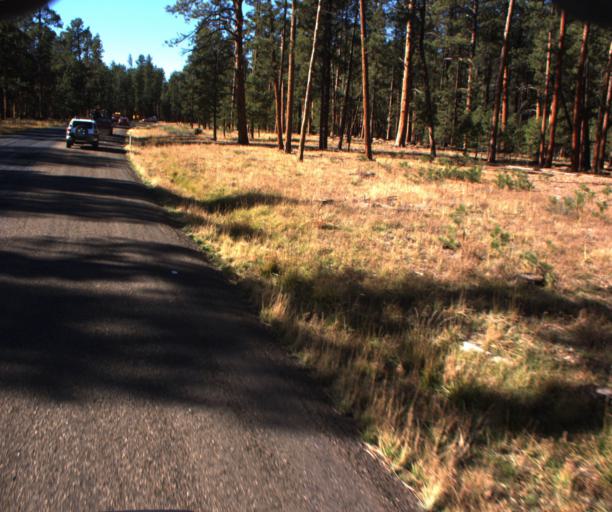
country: US
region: Arizona
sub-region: Coconino County
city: Fredonia
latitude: 36.7186
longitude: -112.2032
